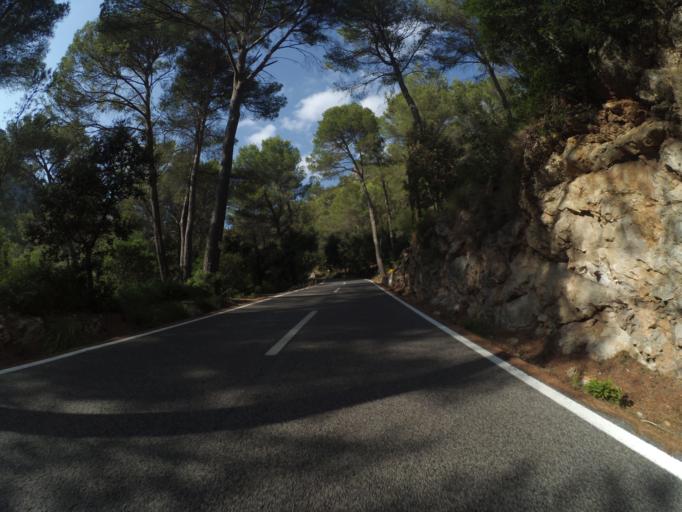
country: ES
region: Balearic Islands
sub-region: Illes Balears
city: Selva
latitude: 39.7839
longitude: 2.8961
